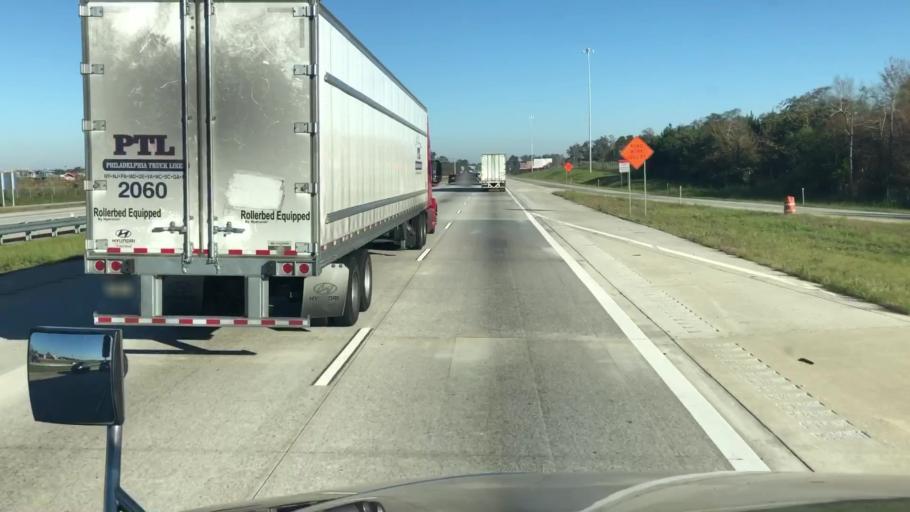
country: US
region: Georgia
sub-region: Dooly County
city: Vienna
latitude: 32.0886
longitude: -83.7630
